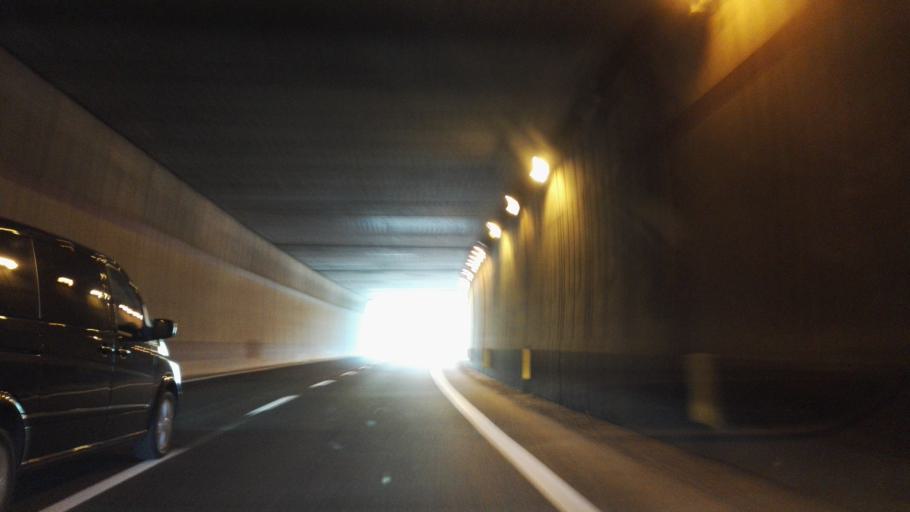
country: IT
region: Lombardy
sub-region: Provincia di Monza e Brianza
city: Lentate sul Seveso
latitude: 45.6738
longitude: 9.1117
